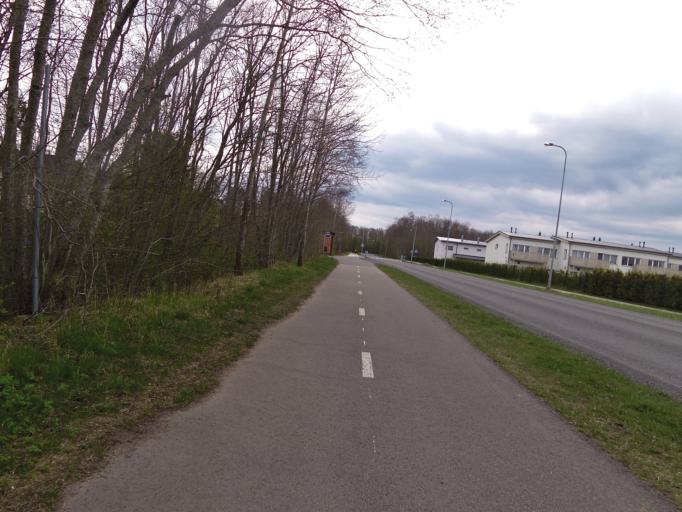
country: EE
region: Harju
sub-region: Kiili vald
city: Kiili
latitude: 59.3659
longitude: 24.8159
